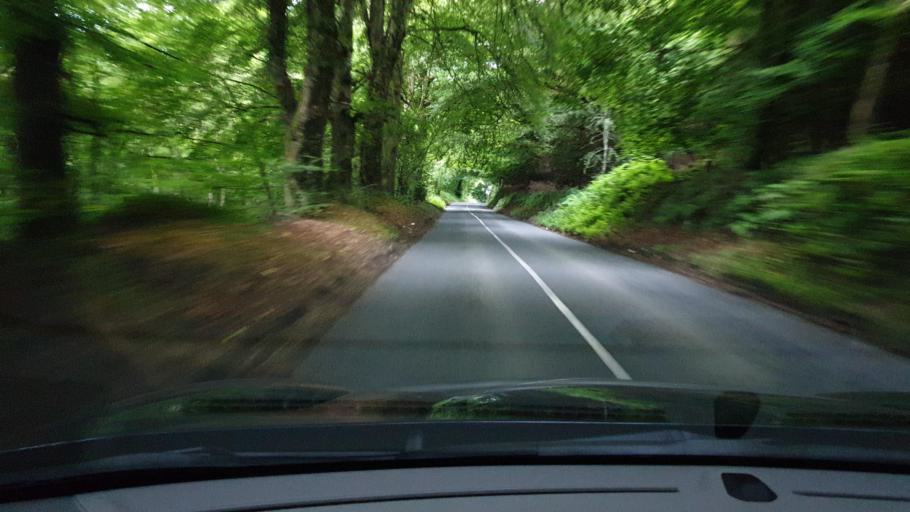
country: IE
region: Leinster
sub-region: South Dublin
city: Saggart
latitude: 53.2588
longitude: -6.4504
